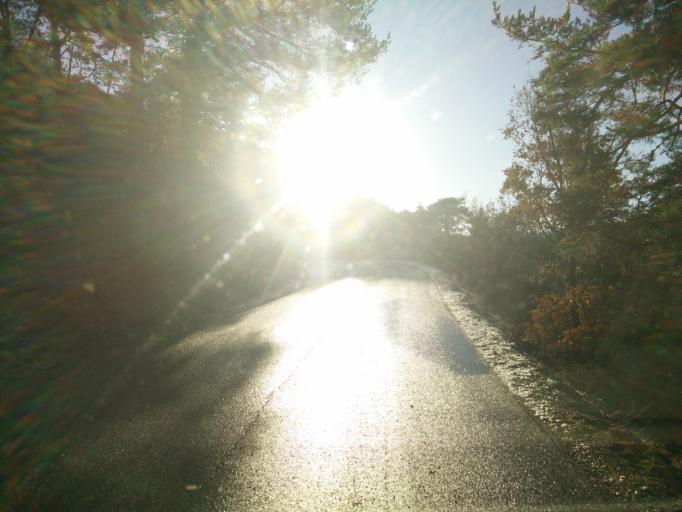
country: FR
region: Provence-Alpes-Cote d'Azur
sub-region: Departement des Alpes-de-Haute-Provence
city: Castellane
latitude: 43.7880
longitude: 6.3754
